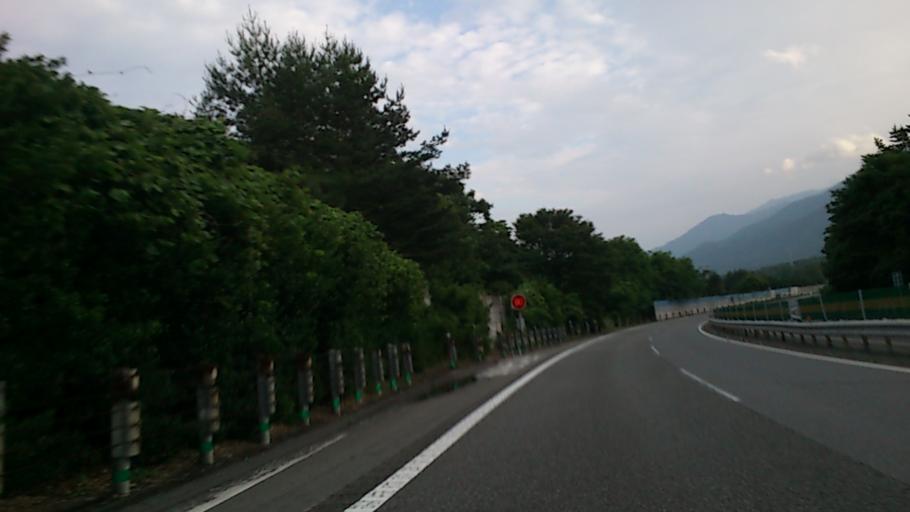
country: JP
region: Nagano
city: Ina
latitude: 35.7572
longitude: 137.9167
